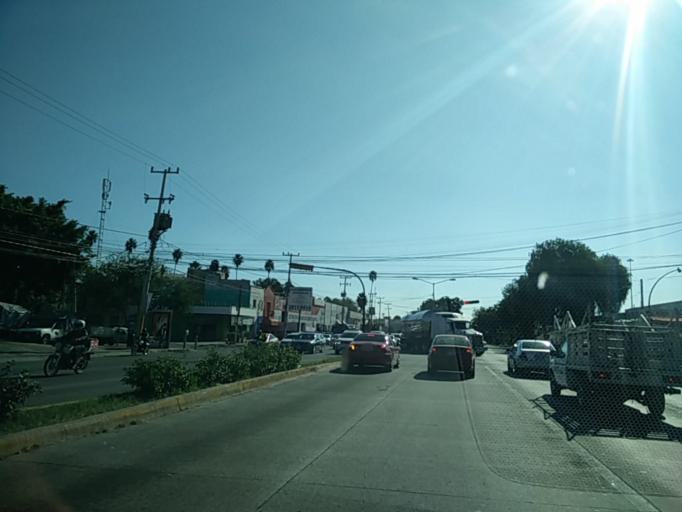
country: MX
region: Jalisco
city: Guadalajara
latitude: 20.6613
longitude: -103.3616
